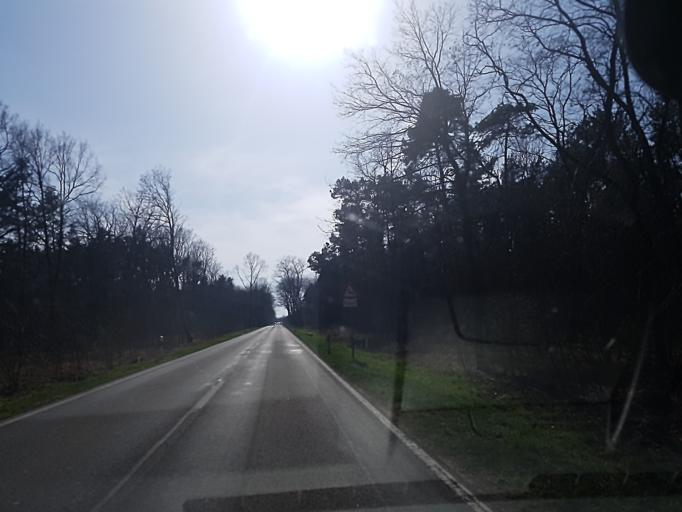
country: DE
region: Brandenburg
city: Vetschau
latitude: 51.7705
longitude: 14.0214
